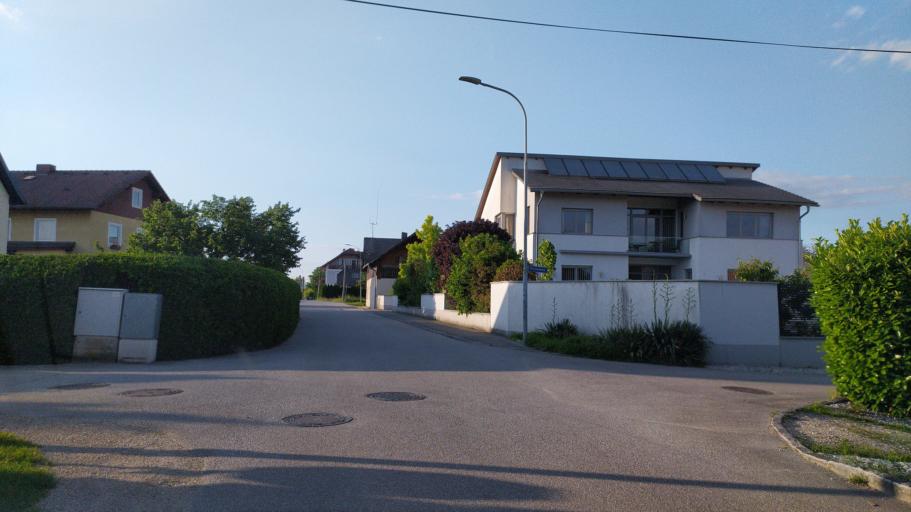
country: AT
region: Lower Austria
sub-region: Politischer Bezirk Amstetten
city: Ennsdorf
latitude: 48.2130
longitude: 14.5693
